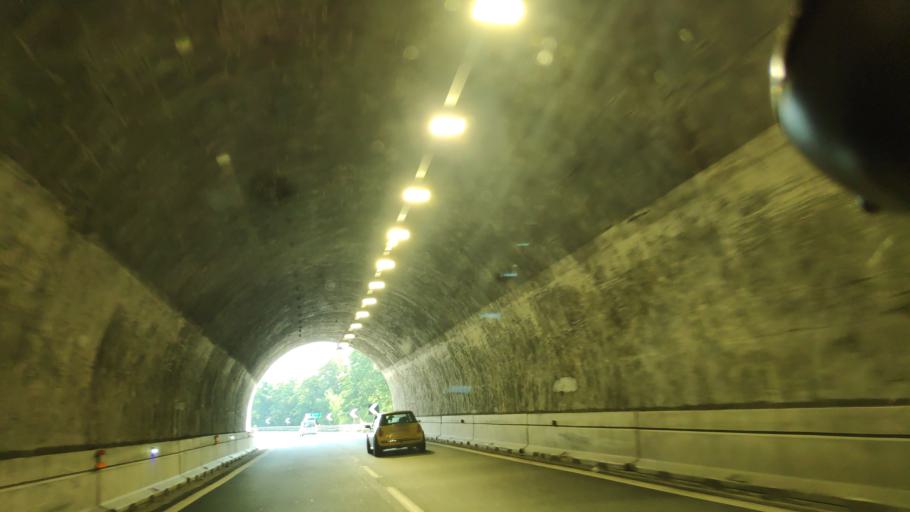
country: IT
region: Calabria
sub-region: Provincia di Cosenza
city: Altilia
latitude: 39.1257
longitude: 16.2620
